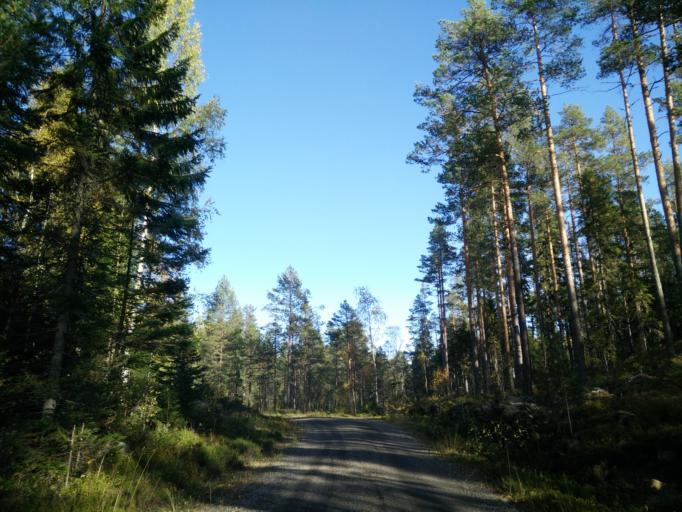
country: SE
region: Vaesternorrland
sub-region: Sundsvalls Kommun
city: Matfors
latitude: 62.3356
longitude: 16.8692
